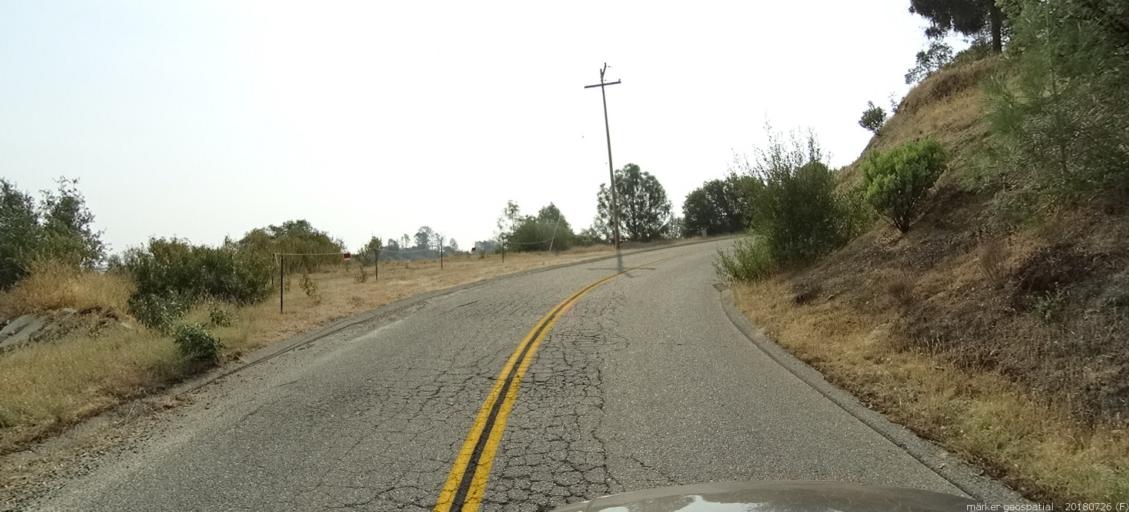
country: US
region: California
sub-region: Madera County
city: Coarsegold
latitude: 37.2002
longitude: -119.6954
